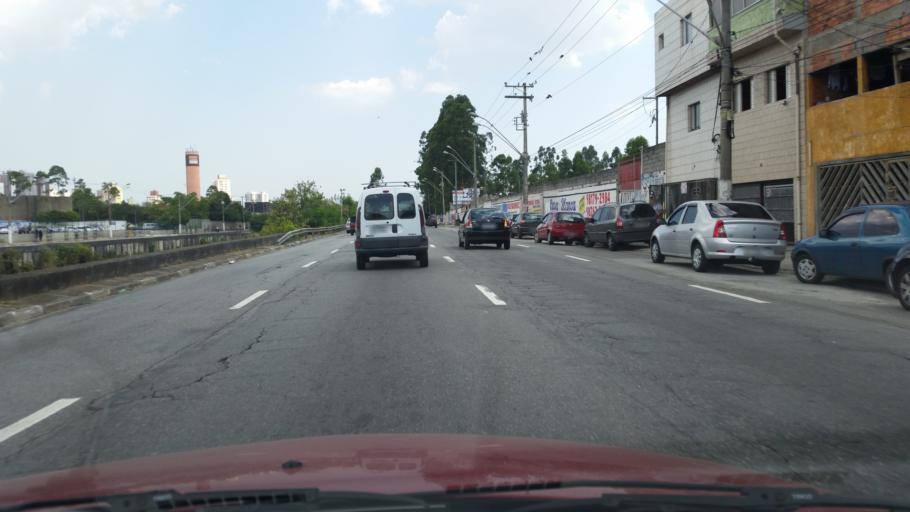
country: BR
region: Sao Paulo
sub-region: Sao Caetano Do Sul
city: Sao Caetano do Sul
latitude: -23.6279
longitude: -46.5399
